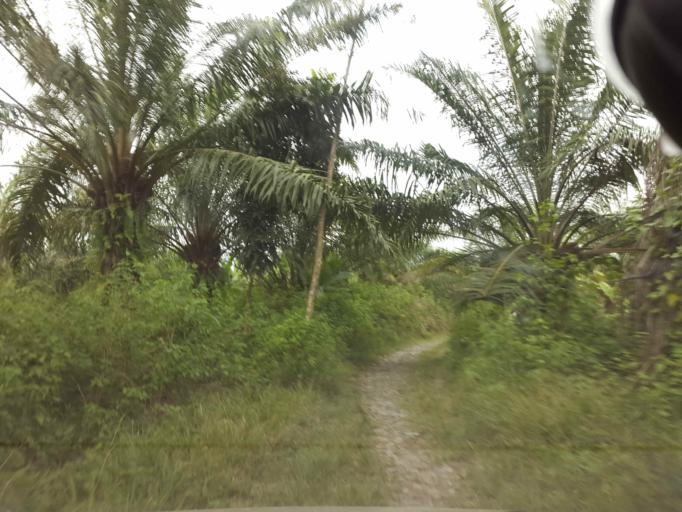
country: ID
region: Lampung
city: Palas
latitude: -5.6792
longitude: 105.7065
